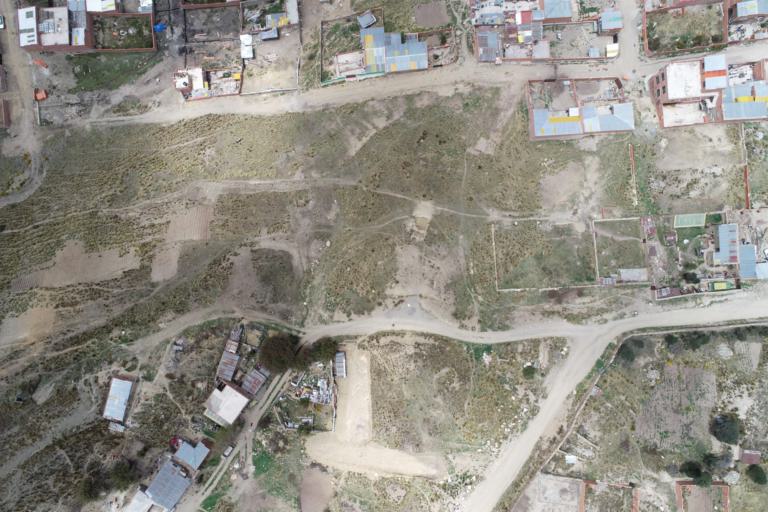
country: BO
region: La Paz
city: La Paz
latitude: -16.4438
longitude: -68.1424
